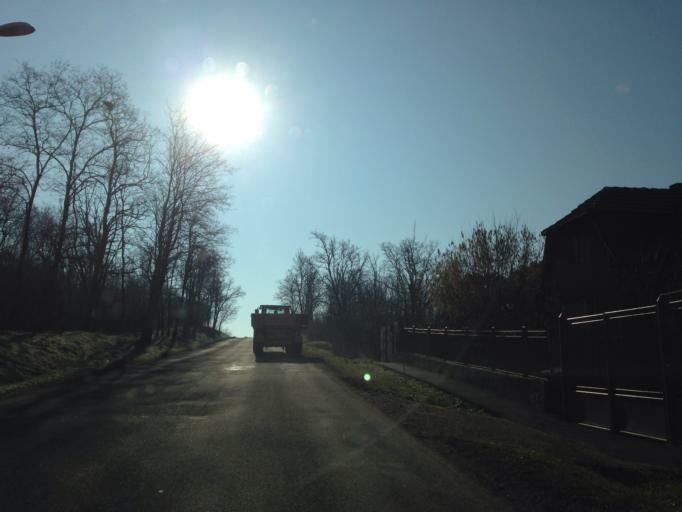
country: SK
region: Nitriansky
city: Svodin
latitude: 47.9486
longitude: 18.4134
